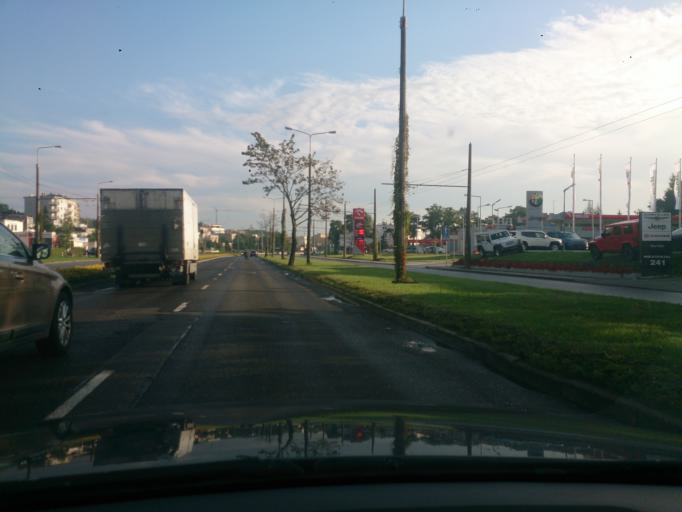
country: PL
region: Pomeranian Voivodeship
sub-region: Gdynia
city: Wielki Kack
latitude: 54.4736
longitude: 18.5146
